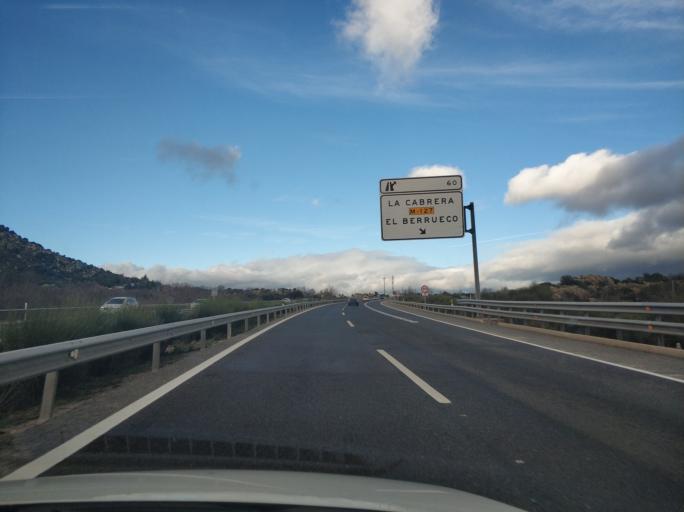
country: ES
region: Madrid
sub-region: Provincia de Madrid
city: La Cabrera
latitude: 40.8708
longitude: -3.6046
